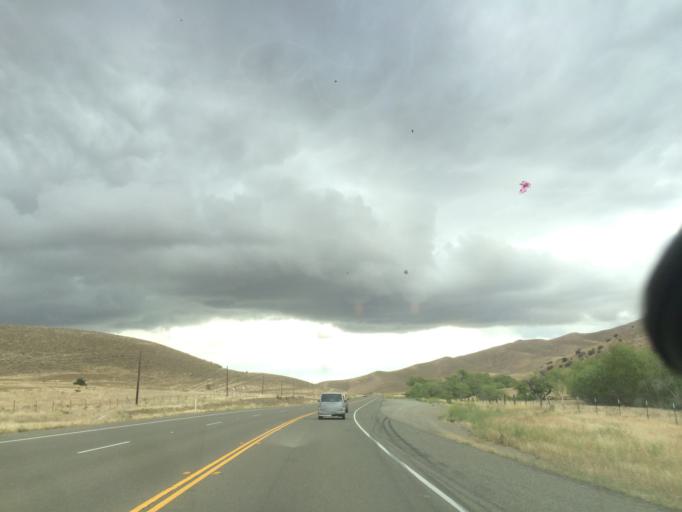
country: US
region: California
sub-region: Kings County
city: Avenal
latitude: 35.7750
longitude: -120.1517
